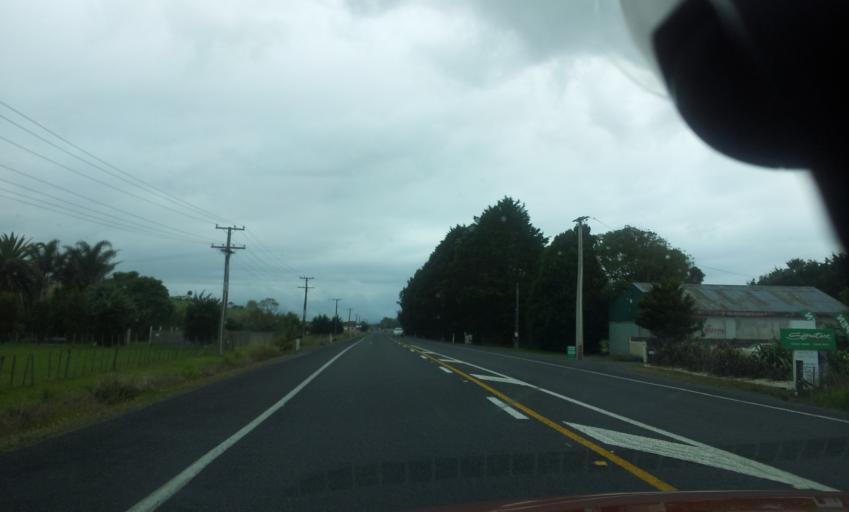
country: NZ
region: Northland
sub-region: Whangarei
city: Ruakaka
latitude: -35.8979
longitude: 174.4411
